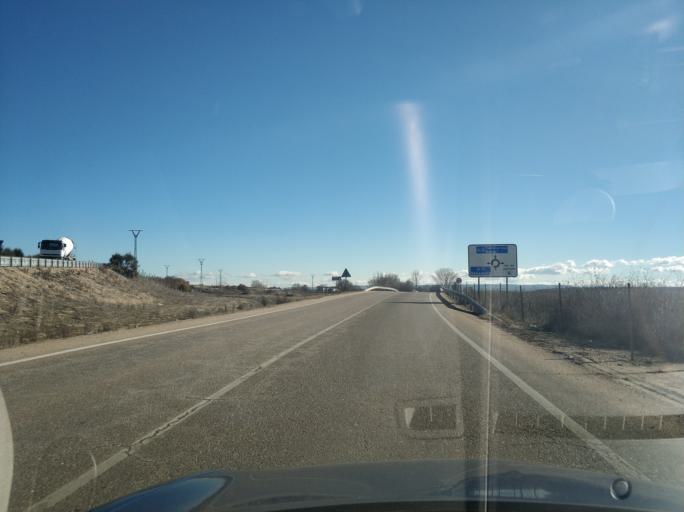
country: ES
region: Castille and Leon
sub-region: Provincia de Valladolid
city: Cisterniga
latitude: 41.5997
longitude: -4.6627
